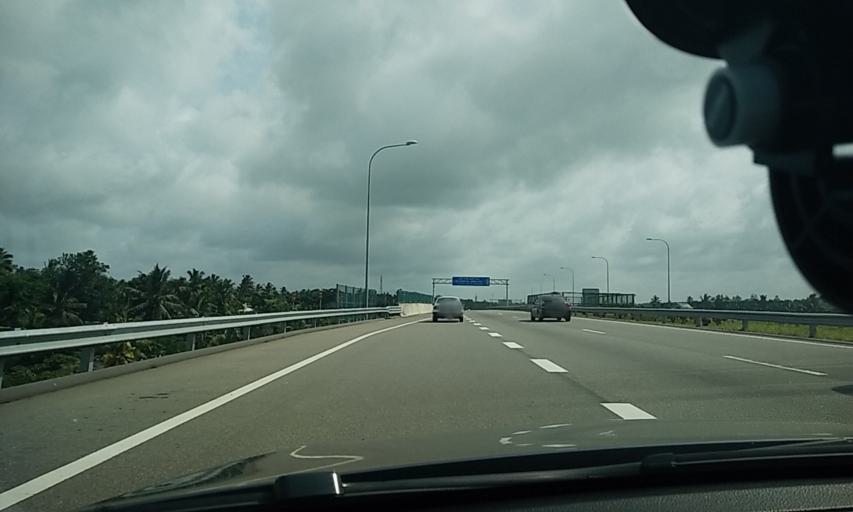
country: LK
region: Western
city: Homagama
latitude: 6.8427
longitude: 79.9797
